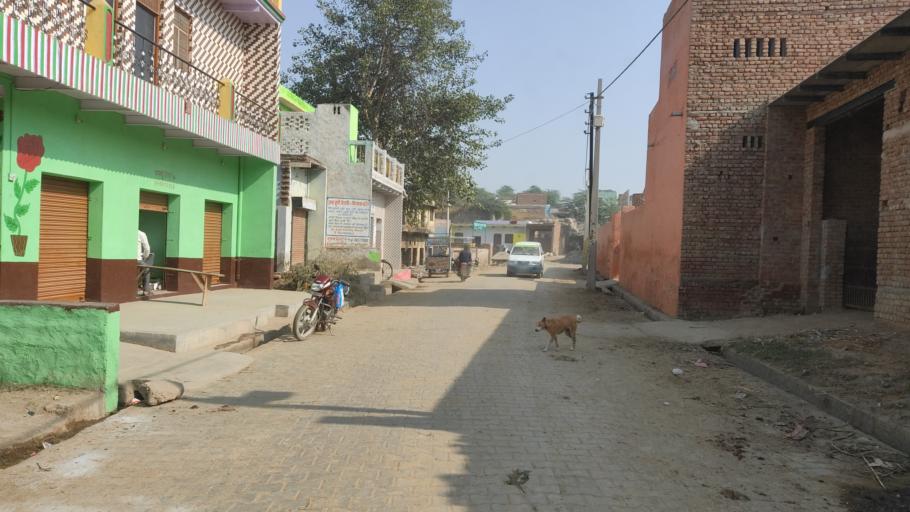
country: IN
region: Uttar Pradesh
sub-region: Mathura
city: Radha Kund
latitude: 27.5572
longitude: 77.5588
